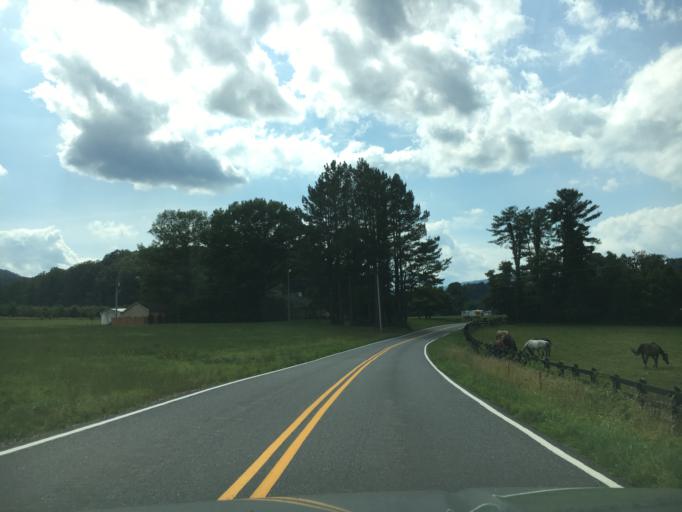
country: US
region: Virginia
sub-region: Roanoke County
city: Narrows
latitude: 37.1378
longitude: -79.9803
